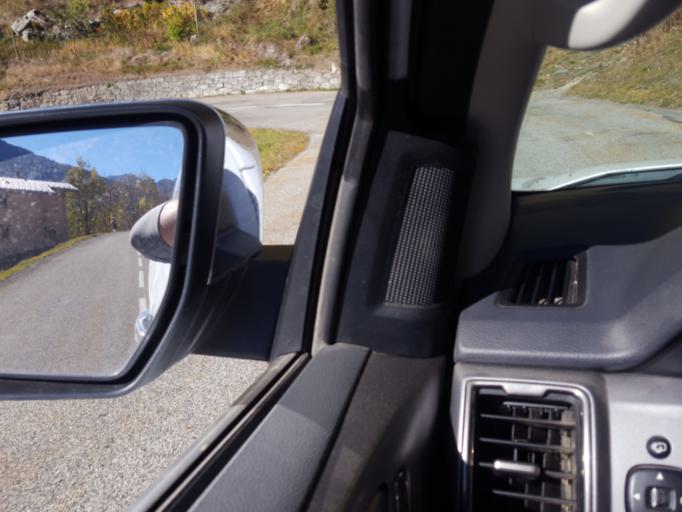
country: FR
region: Rhone-Alpes
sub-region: Departement de la Savoie
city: Modane
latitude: 45.2066
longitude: 6.6344
